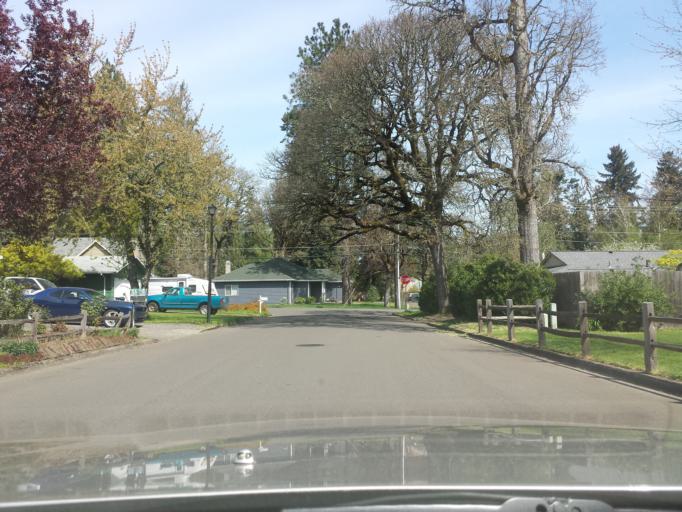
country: US
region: Oregon
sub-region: Washington County
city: Aloha
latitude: 45.4990
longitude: -122.8580
